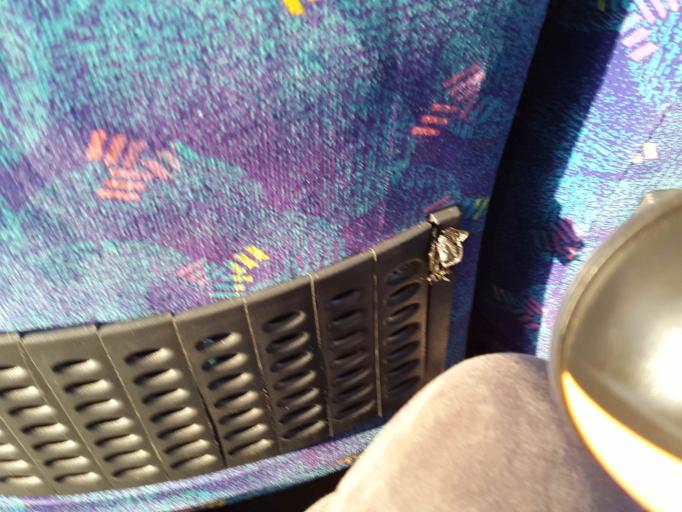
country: ID
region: Central Java
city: Ceper
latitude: -7.6744
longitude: 110.6538
